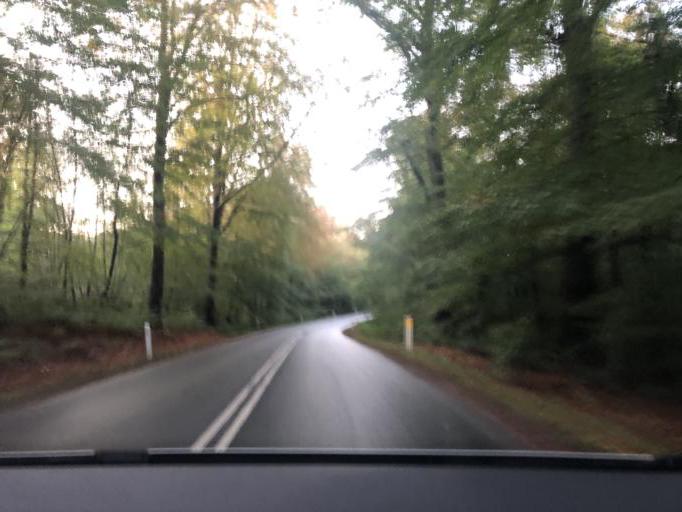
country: DK
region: Capital Region
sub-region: Egedal Kommune
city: Stenlose
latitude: 55.8104
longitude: 12.2095
